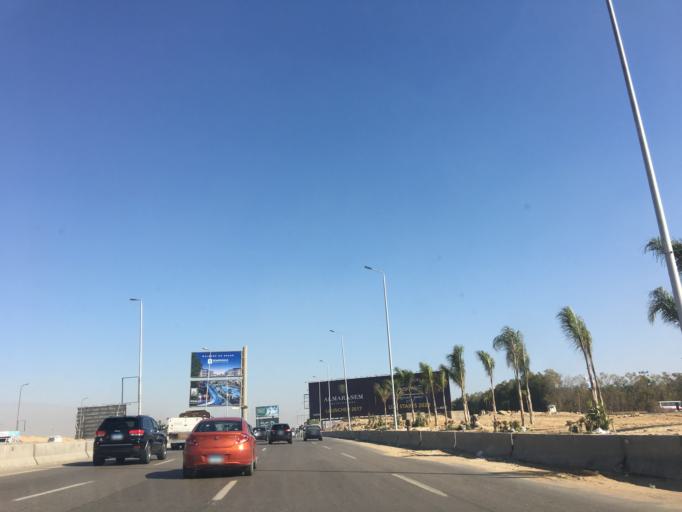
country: EG
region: Muhafazat al Qalyubiyah
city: Al Khankah
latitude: 30.0575
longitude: 31.4148
